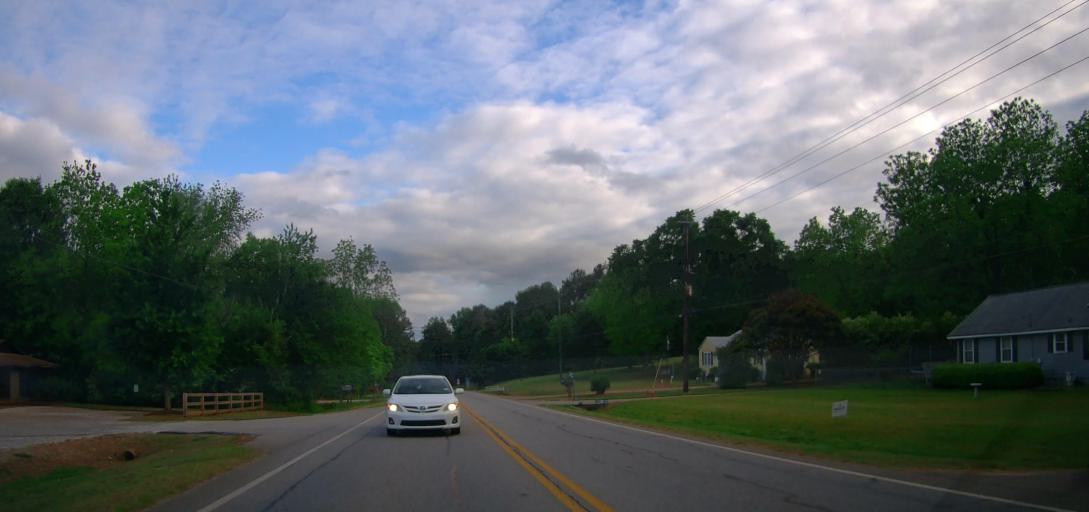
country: US
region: Georgia
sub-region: Oconee County
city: Watkinsville
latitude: 33.8762
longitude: -83.4126
